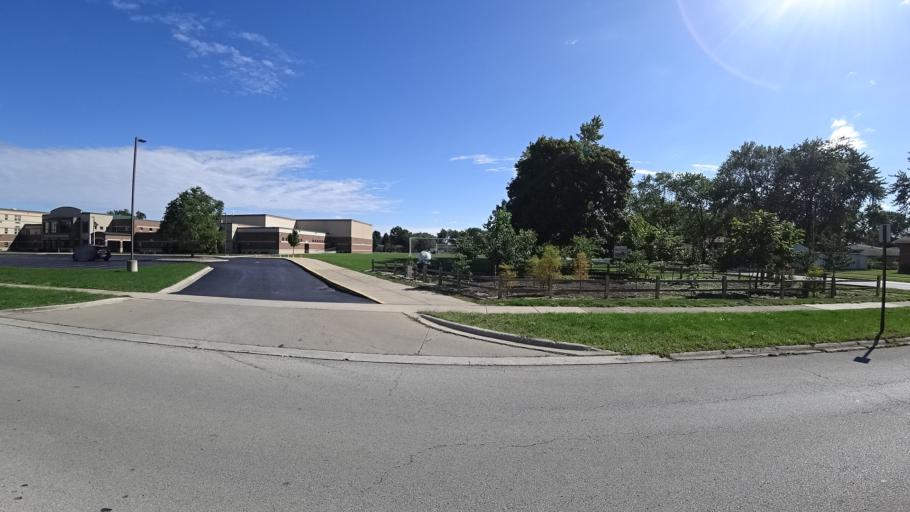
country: US
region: Illinois
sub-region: Cook County
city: Oak Lawn
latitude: 41.7125
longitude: -87.7548
